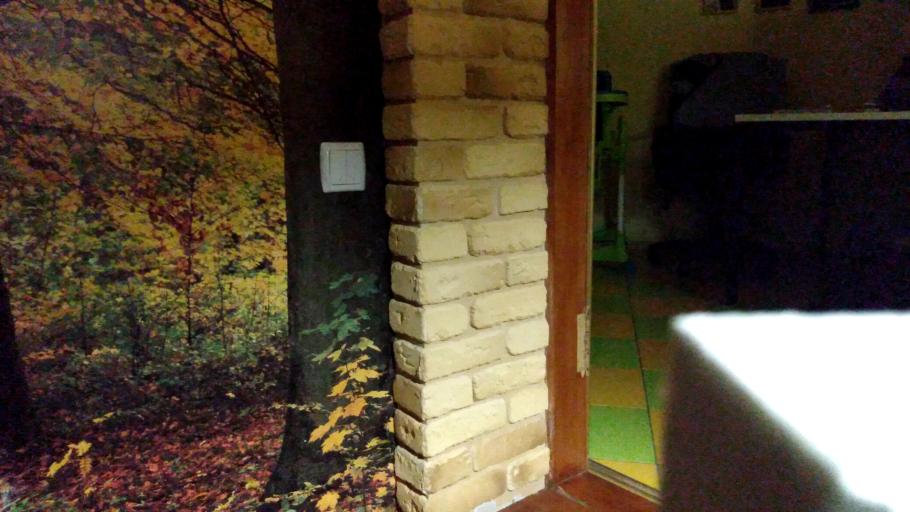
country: RU
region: Vologda
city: Lipin Bor
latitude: 61.1418
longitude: 37.9096
